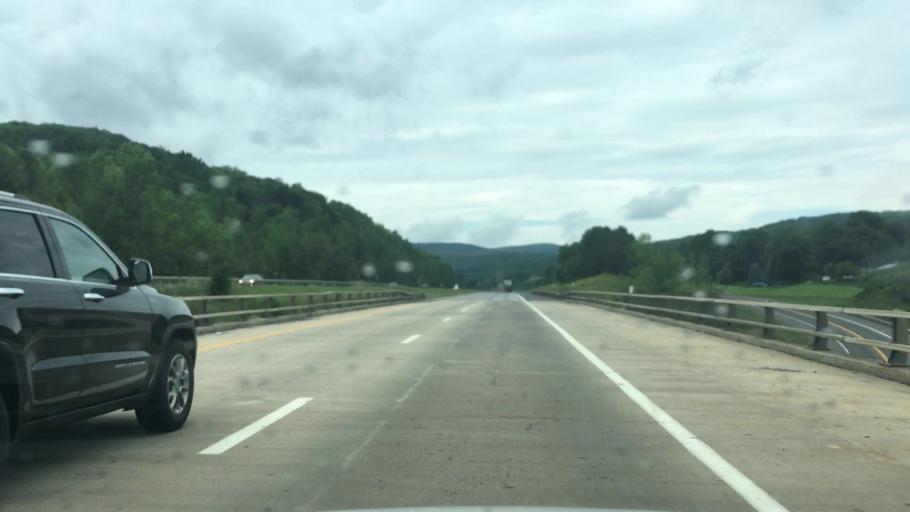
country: US
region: New York
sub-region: Schoharie County
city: Cobleskill
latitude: 42.6448
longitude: -74.5890
